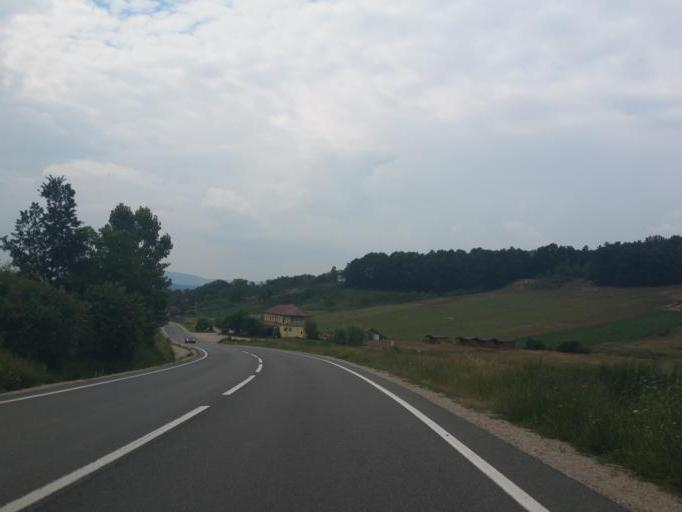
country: RO
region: Salaj
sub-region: Comuna Romanasi
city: Romanasi
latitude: 47.0769
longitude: 23.2042
